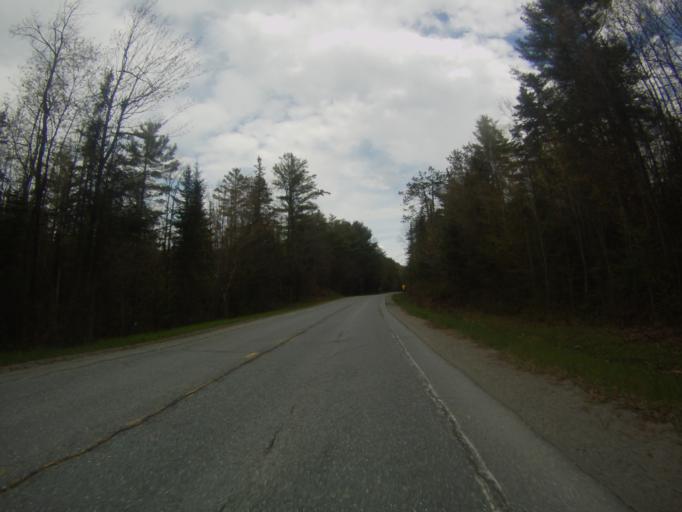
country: US
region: New York
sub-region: Essex County
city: Mineville
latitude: 44.0973
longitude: -73.5596
